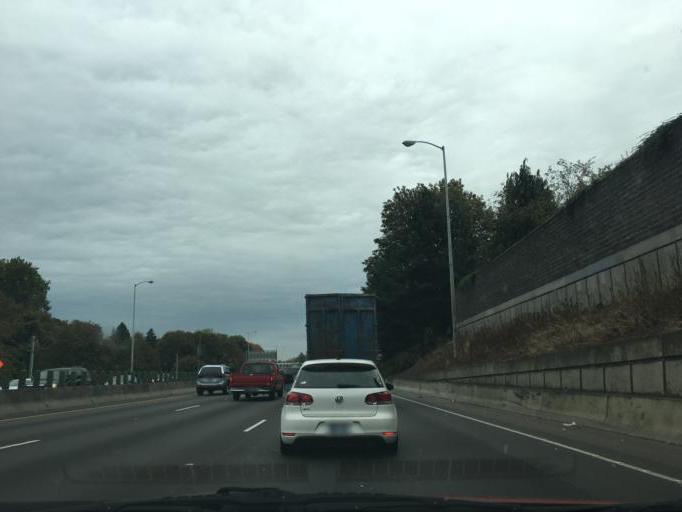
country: US
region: Oregon
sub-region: Multnomah County
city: Portland
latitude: 45.5299
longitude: -122.6440
